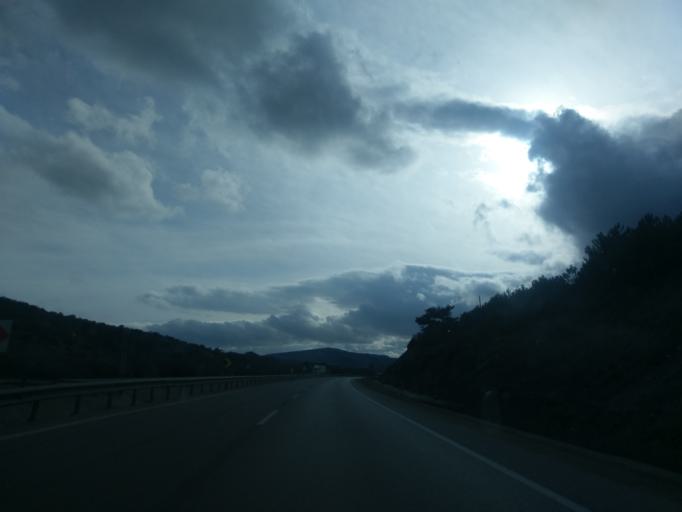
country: TR
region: Kuetahya
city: Sabuncu
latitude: 39.5502
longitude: 30.0607
